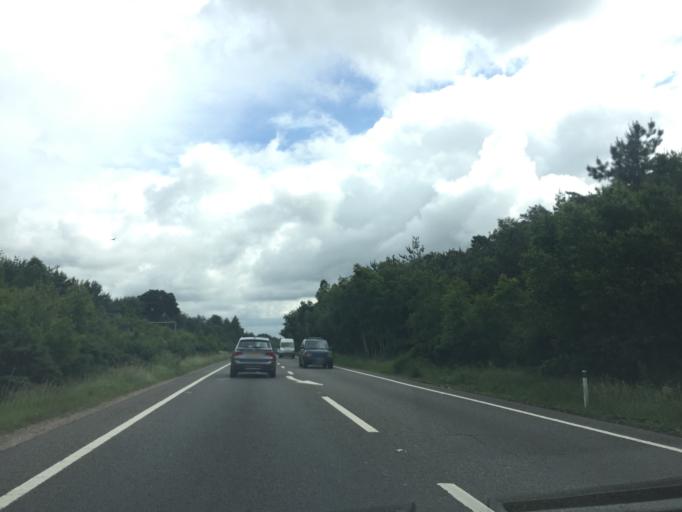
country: GB
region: England
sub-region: Dorset
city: Ferndown
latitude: 50.8110
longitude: -1.9273
